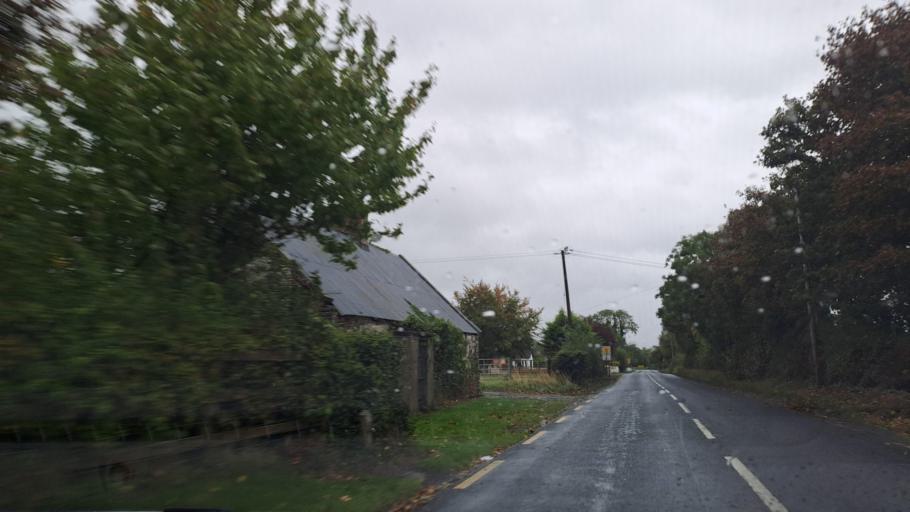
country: IE
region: Leinster
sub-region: Lu
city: Ardee
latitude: 53.9733
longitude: -6.5329
